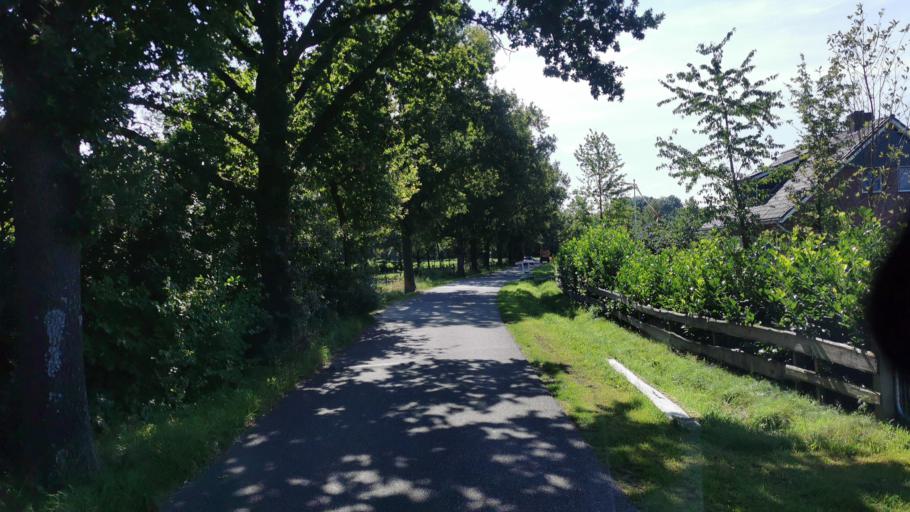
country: NL
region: Overijssel
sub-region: Gemeente Enschede
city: Enschede
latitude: 52.2012
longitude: 6.9582
